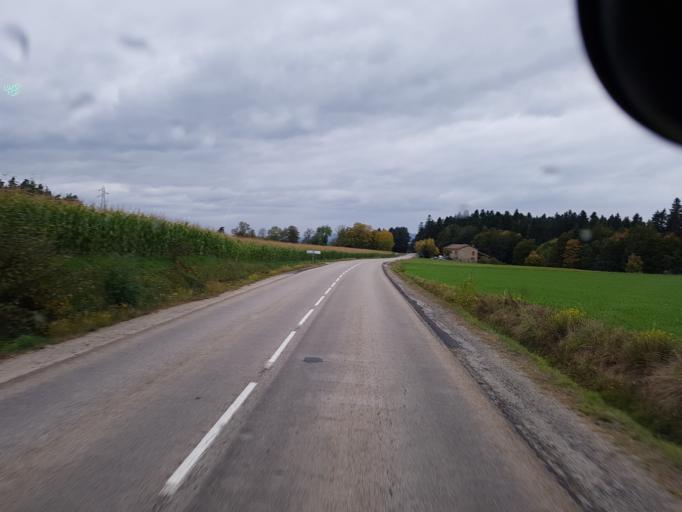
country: FR
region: Auvergne
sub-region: Departement de la Haute-Loire
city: Sainte-Sigolene
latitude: 45.2329
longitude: 4.2219
